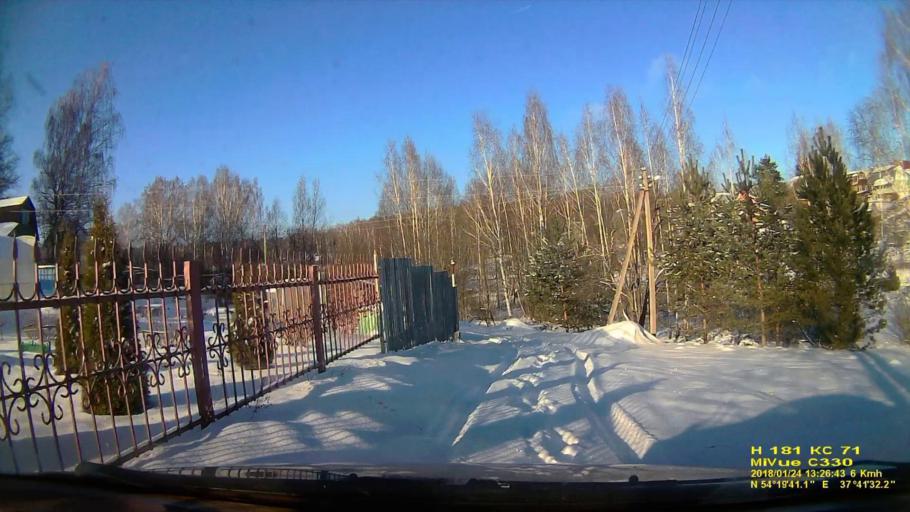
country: RU
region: Tula
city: Revyakino
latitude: 54.3281
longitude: 37.6923
